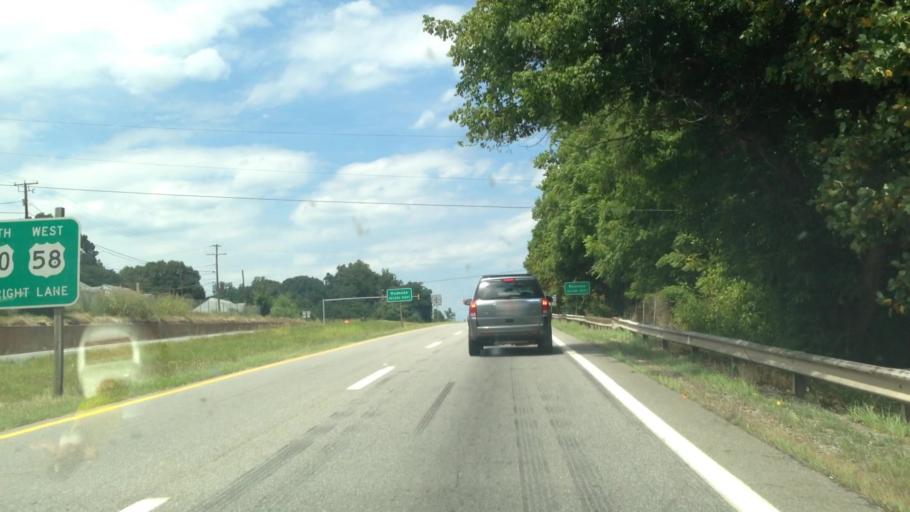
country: US
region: Virginia
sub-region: Henry County
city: Chatmoss
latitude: 36.6199
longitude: -79.8602
